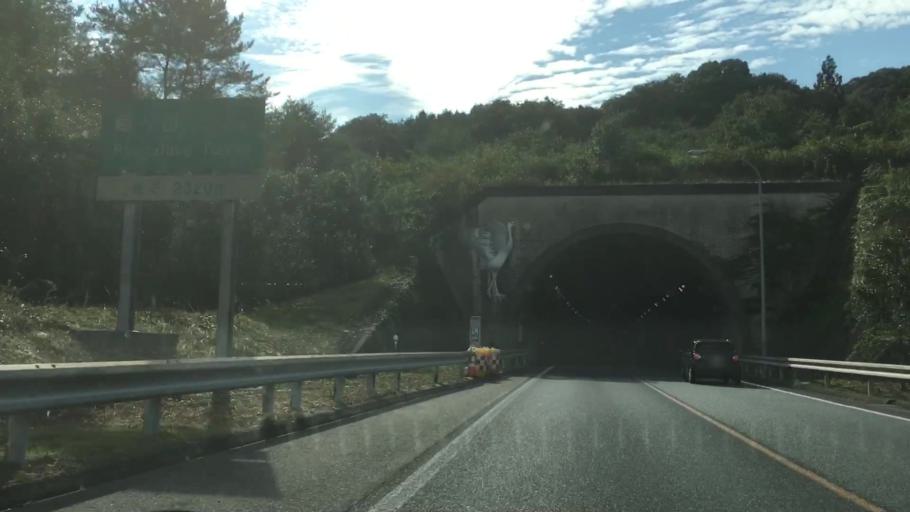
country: JP
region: Yamaguchi
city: Yanai
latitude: 34.0623
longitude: 132.0416
